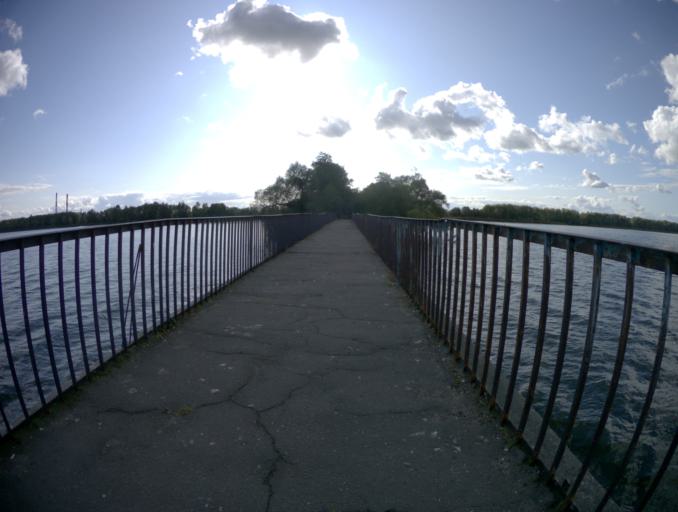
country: RU
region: Moskovskaya
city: Kerva
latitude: 55.5994
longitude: 39.5664
